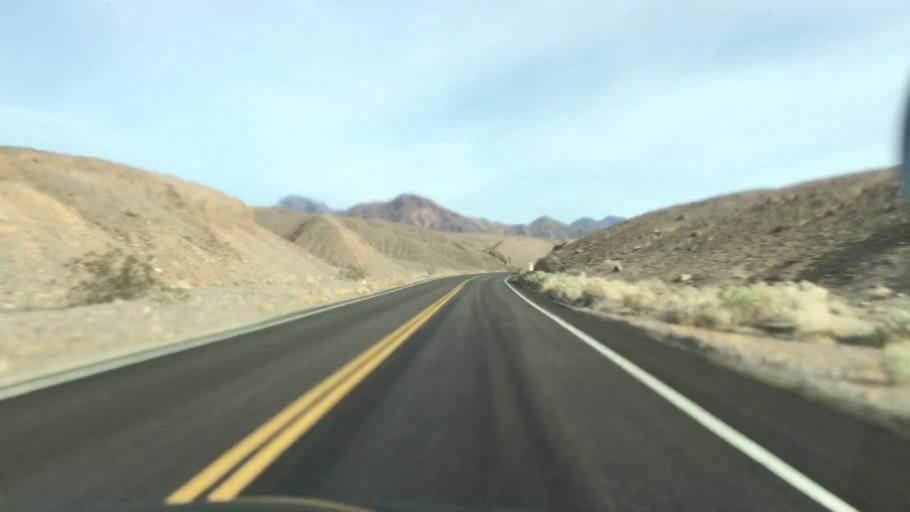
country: US
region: Nevada
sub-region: Nye County
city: Beatty
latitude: 36.6643
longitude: -117.0184
